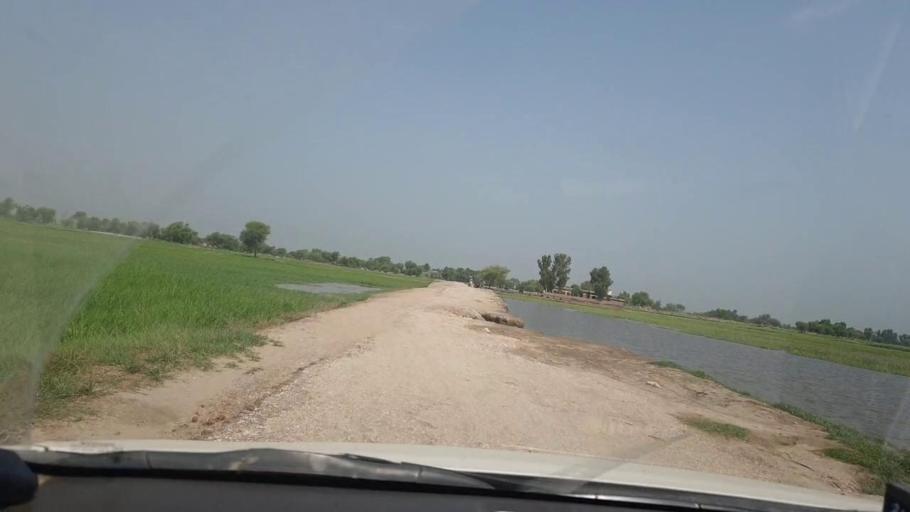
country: PK
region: Sindh
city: Chak
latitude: 27.8762
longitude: 68.7841
